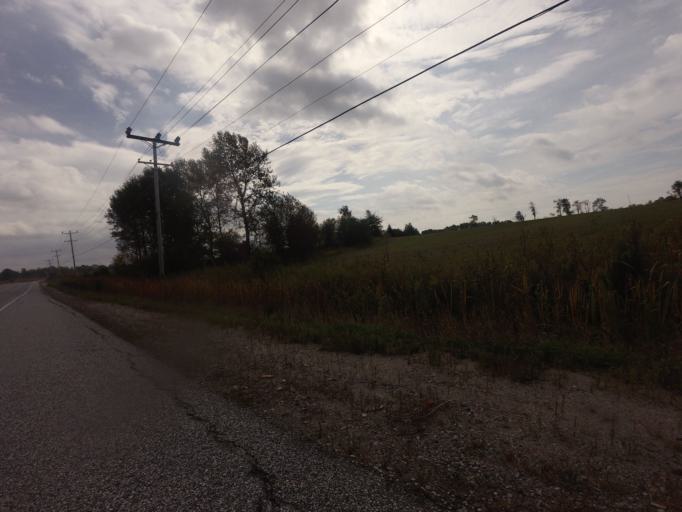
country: CA
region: Quebec
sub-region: Outaouais
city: Wakefield
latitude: 45.8628
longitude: -76.0182
